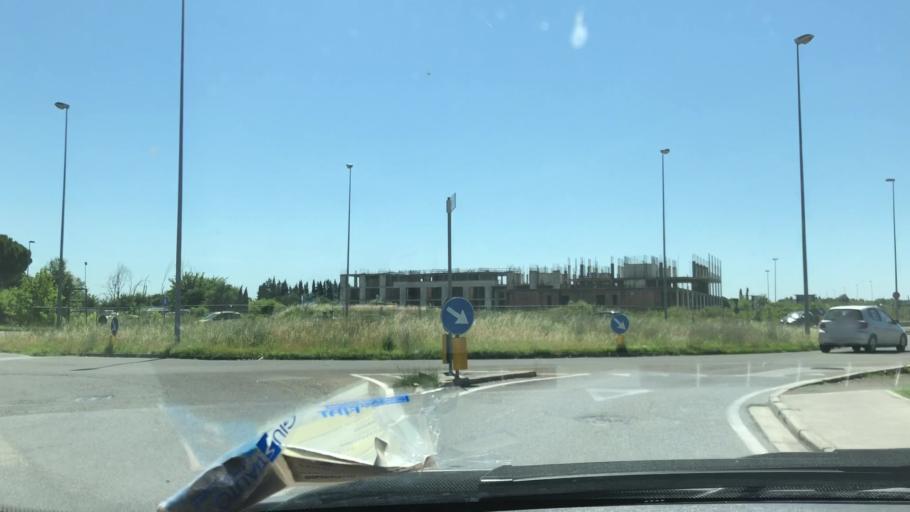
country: IT
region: Tuscany
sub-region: Province of Pisa
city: Pontedera
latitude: 43.6553
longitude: 10.6261
